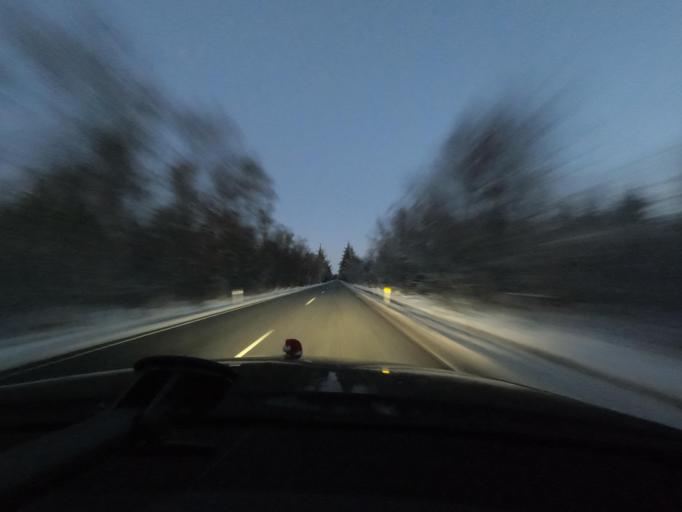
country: DK
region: South Denmark
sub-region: Tonder Kommune
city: Sherrebek
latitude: 55.1747
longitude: 8.8545
